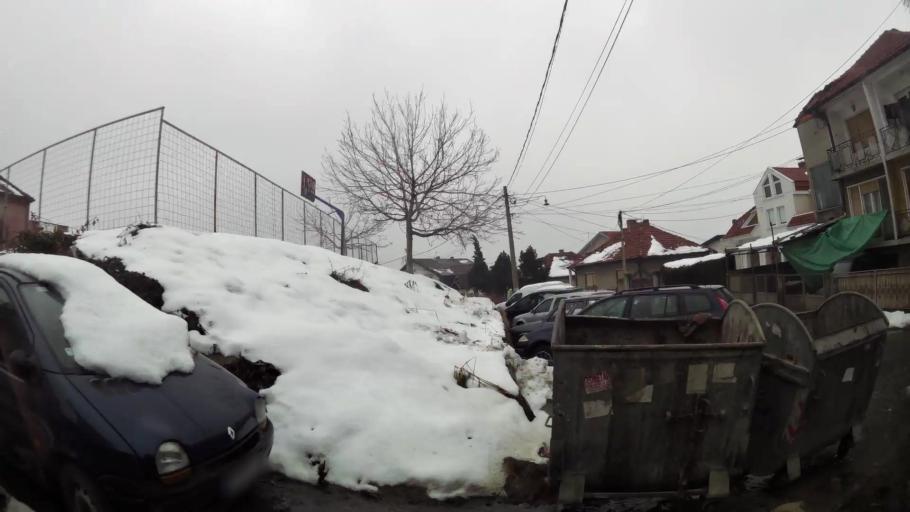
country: RS
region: Central Serbia
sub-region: Belgrade
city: Zvezdara
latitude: 44.7457
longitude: 20.5031
